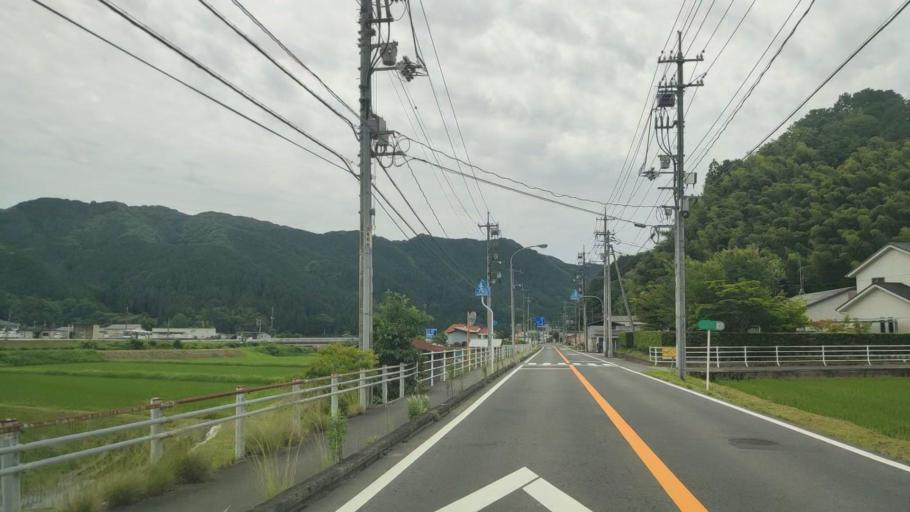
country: JP
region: Hyogo
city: Yamazakicho-nakabirose
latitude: 35.0995
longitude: 134.3238
